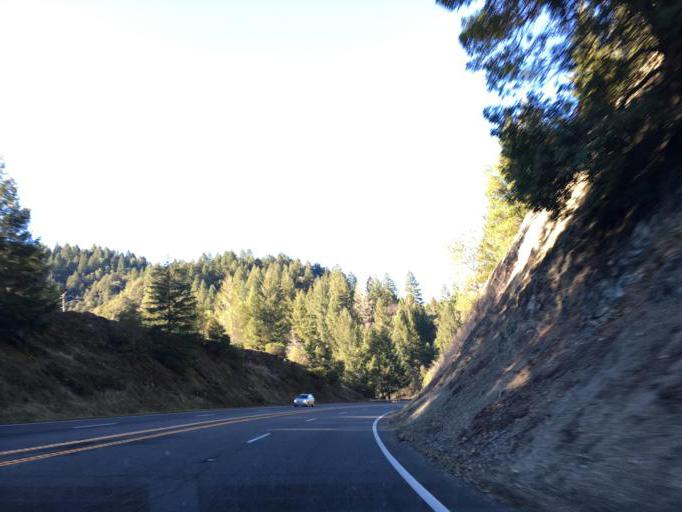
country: US
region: California
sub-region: Mendocino County
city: Laytonville
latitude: 39.5803
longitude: -123.4433
